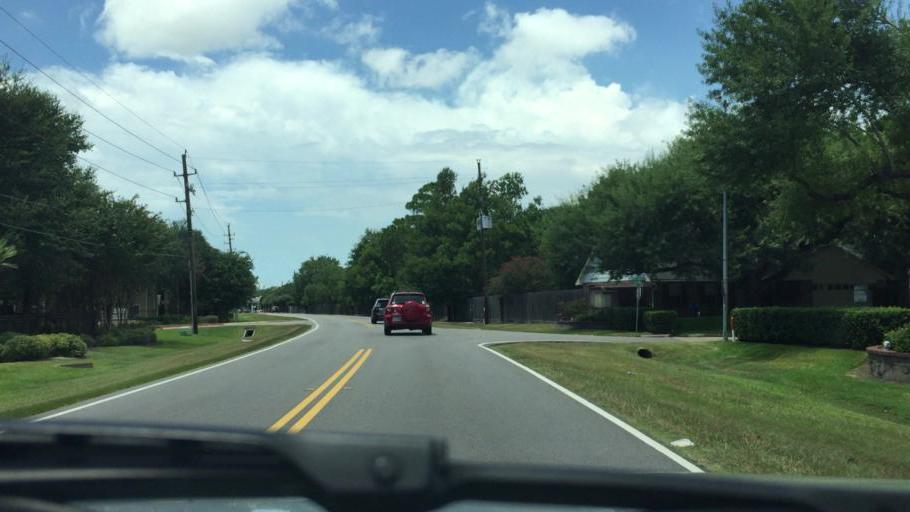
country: US
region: Texas
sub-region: Harris County
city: Jersey Village
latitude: 29.8862
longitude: -95.5438
